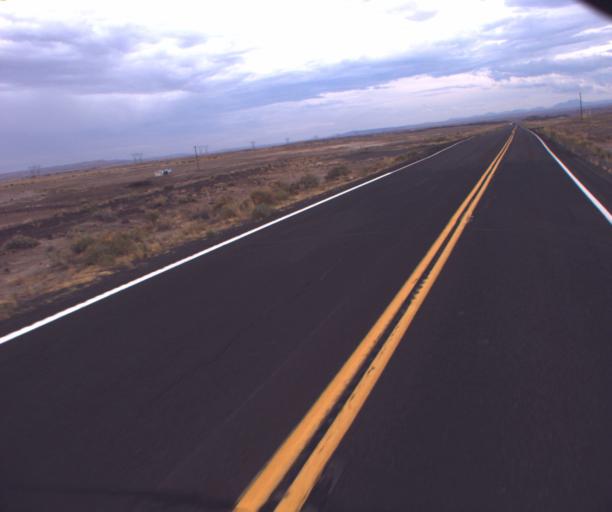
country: US
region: Arizona
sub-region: Coconino County
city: Tuba City
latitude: 35.9567
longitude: -111.3978
